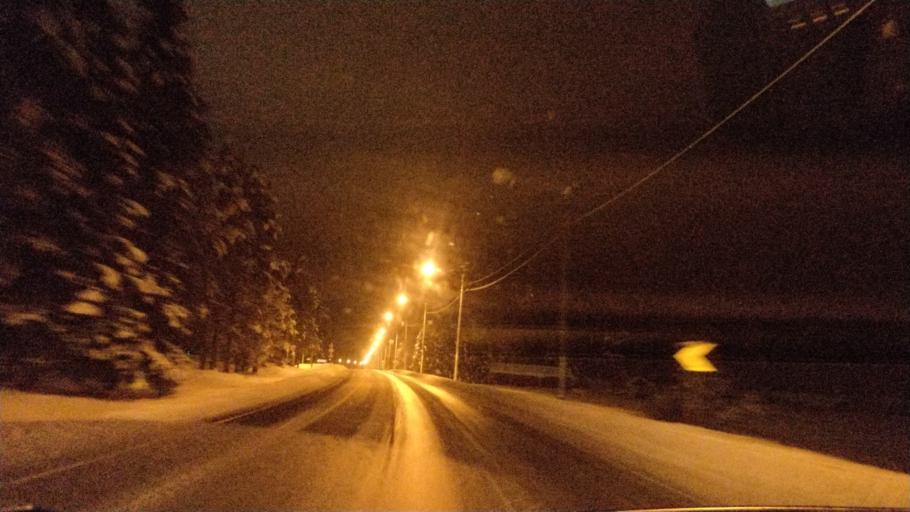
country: FI
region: Lapland
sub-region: Rovaniemi
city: Rovaniemi
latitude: 66.2731
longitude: 25.3296
